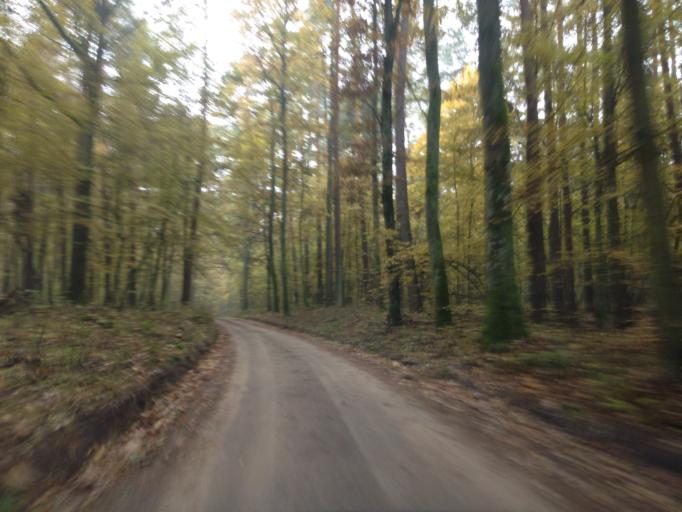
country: PL
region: Kujawsko-Pomorskie
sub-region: Powiat brodnicki
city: Gorzno
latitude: 53.2095
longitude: 19.6804
